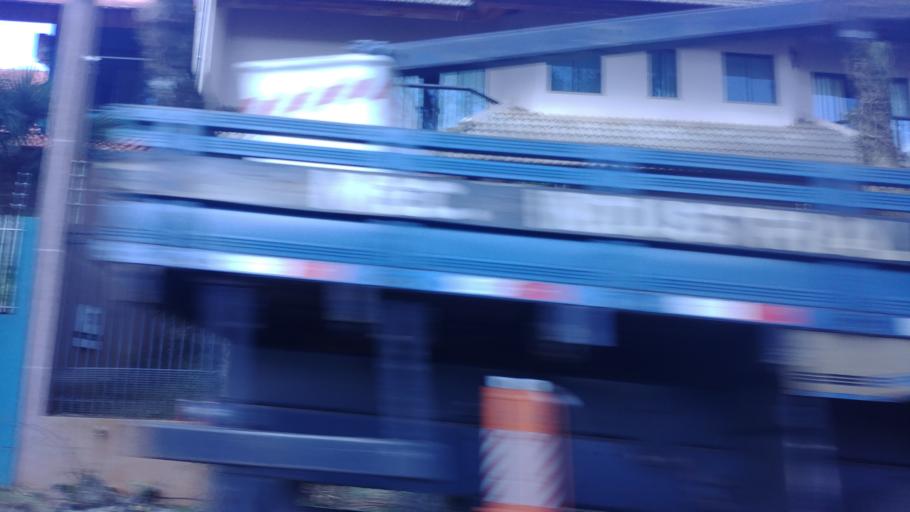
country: BR
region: Parana
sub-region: Guarapuava
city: Guarapuava
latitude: -25.3861
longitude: -51.4658
